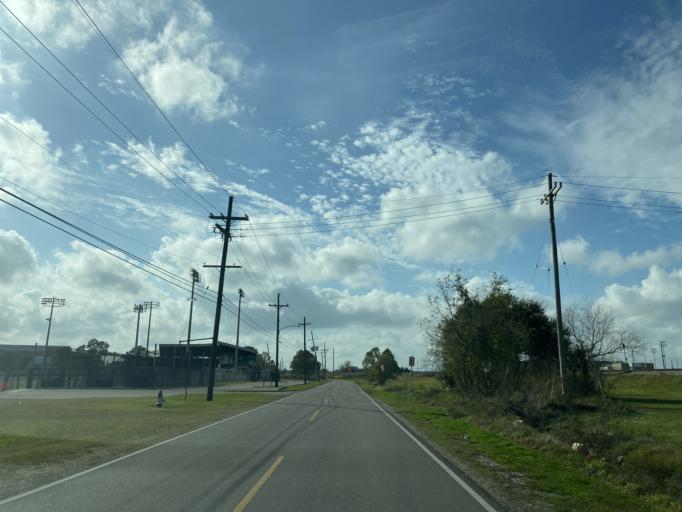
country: US
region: Louisiana
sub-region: Orleans Parish
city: New Orleans
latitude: 30.0293
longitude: -90.0415
